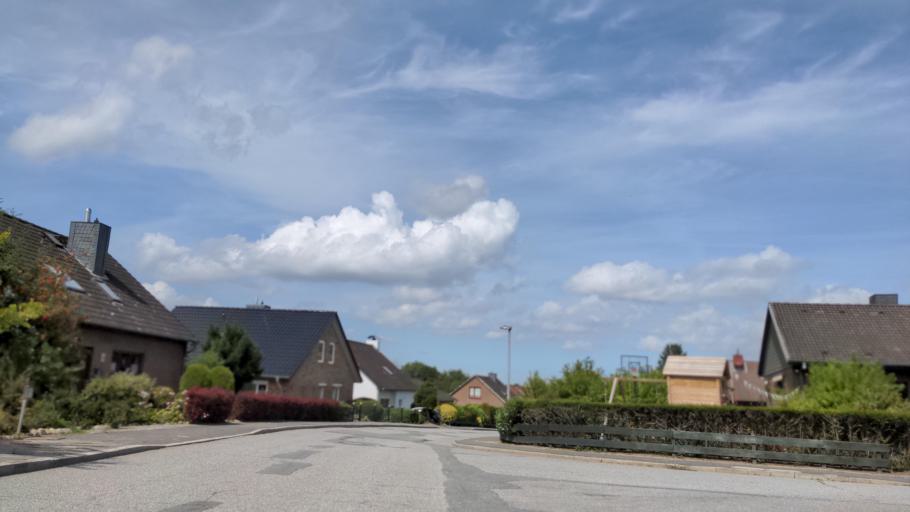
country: DE
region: Schleswig-Holstein
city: Eutin
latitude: 54.1241
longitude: 10.6057
